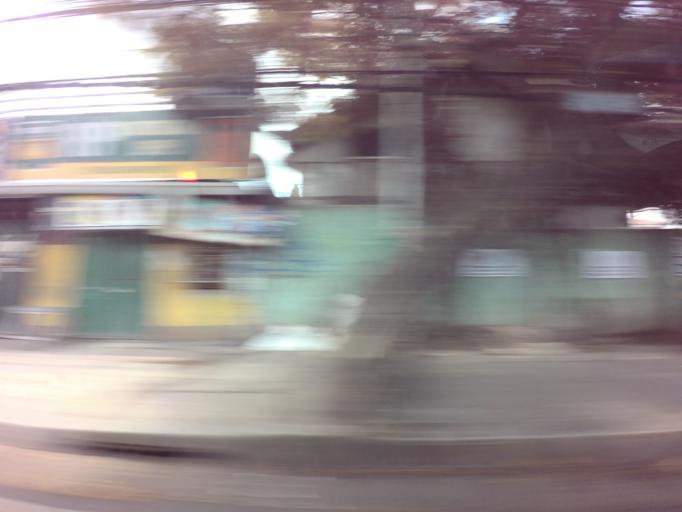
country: PH
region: Calabarzon
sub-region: Province of Laguna
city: San Pedro
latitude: 14.4007
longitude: 121.0470
